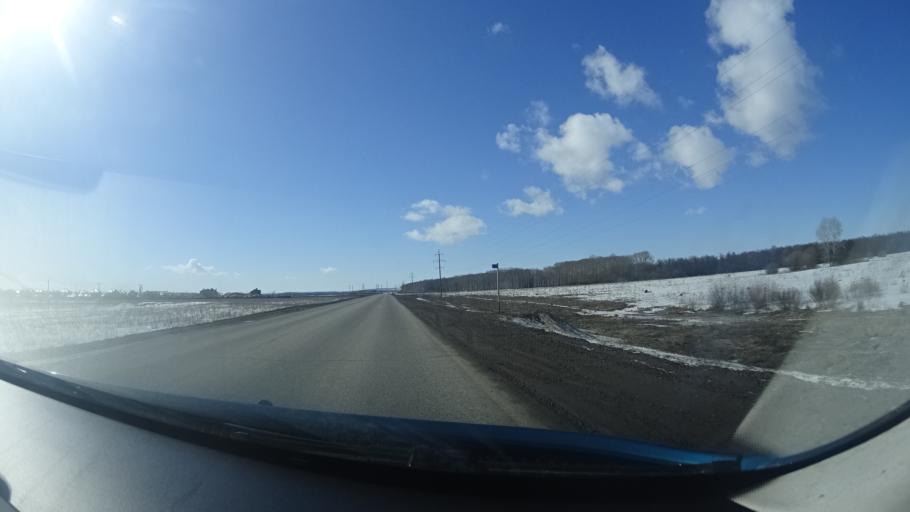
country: RU
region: Bashkortostan
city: Ufa
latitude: 54.6314
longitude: 55.9029
